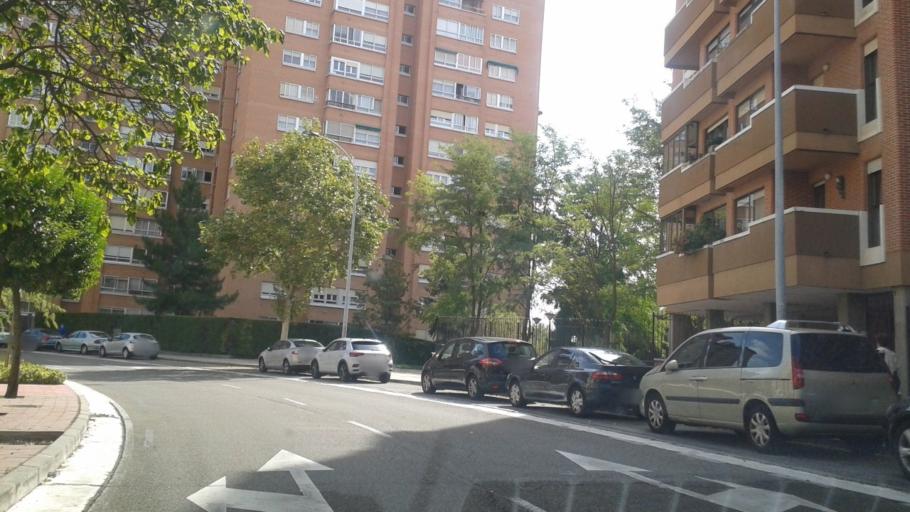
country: ES
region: Castille and Leon
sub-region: Provincia de Valladolid
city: Zaratan
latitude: 41.6338
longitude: -4.7575
